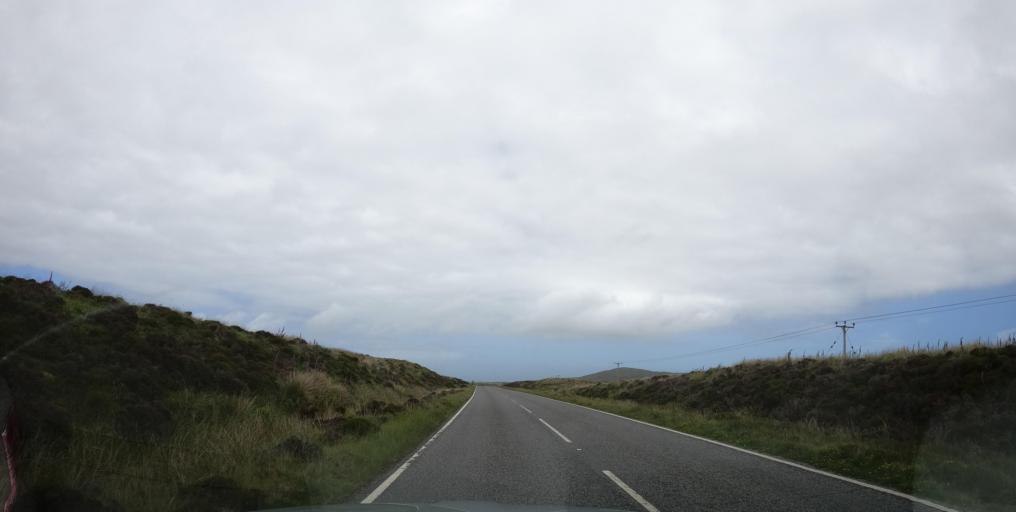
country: GB
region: Scotland
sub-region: Eilean Siar
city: Isle of South Uist
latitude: 57.2739
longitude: -7.3654
